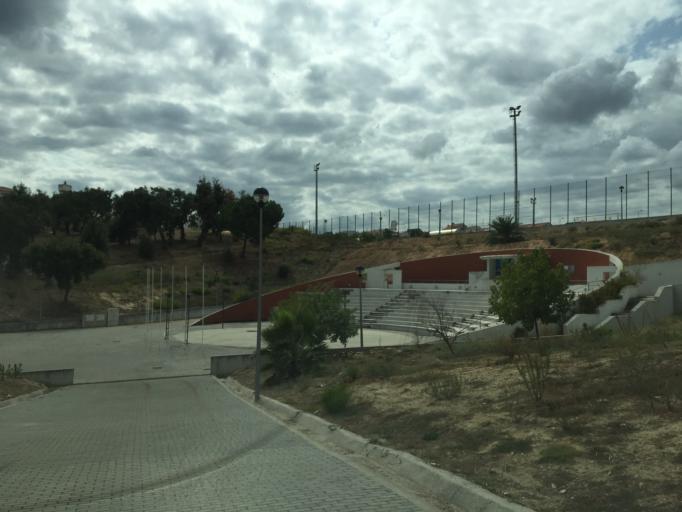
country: PT
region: Portalegre
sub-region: Ponte de Sor
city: Santo Andre
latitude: 39.0816
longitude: -8.1726
